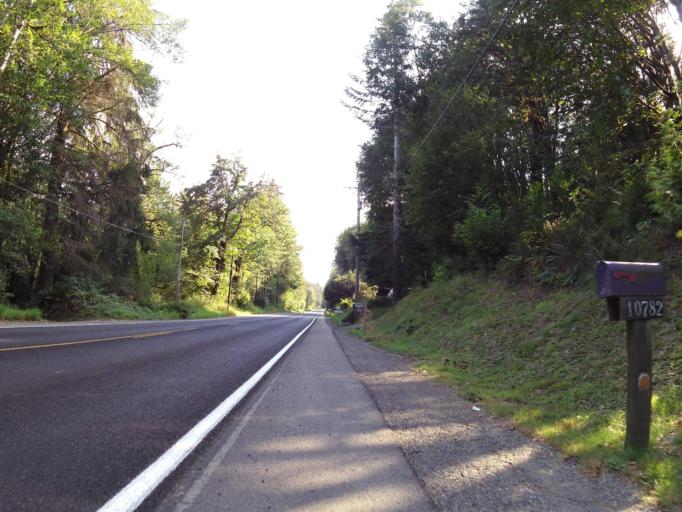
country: US
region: Washington
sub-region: Mason County
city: Belfair
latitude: 47.5088
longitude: -122.7956
